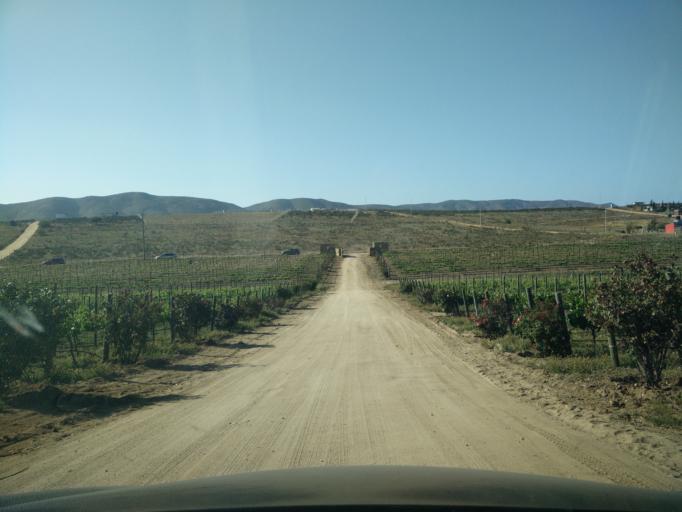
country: MX
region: Baja California
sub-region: Ensenada
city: Rancho Verde
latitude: 32.0176
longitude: -116.6640
